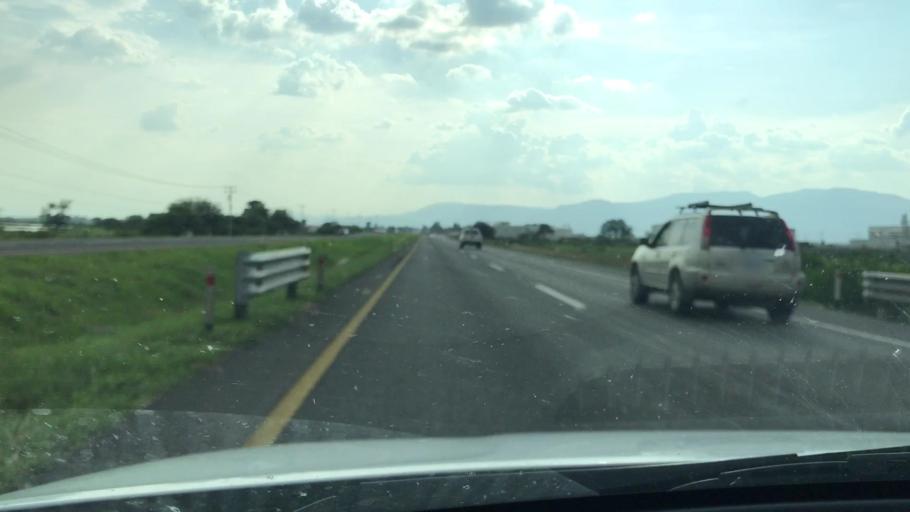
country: MX
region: Guanajuato
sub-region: Penjamo
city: Estacion Corralejo
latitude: 20.4516
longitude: -101.5759
